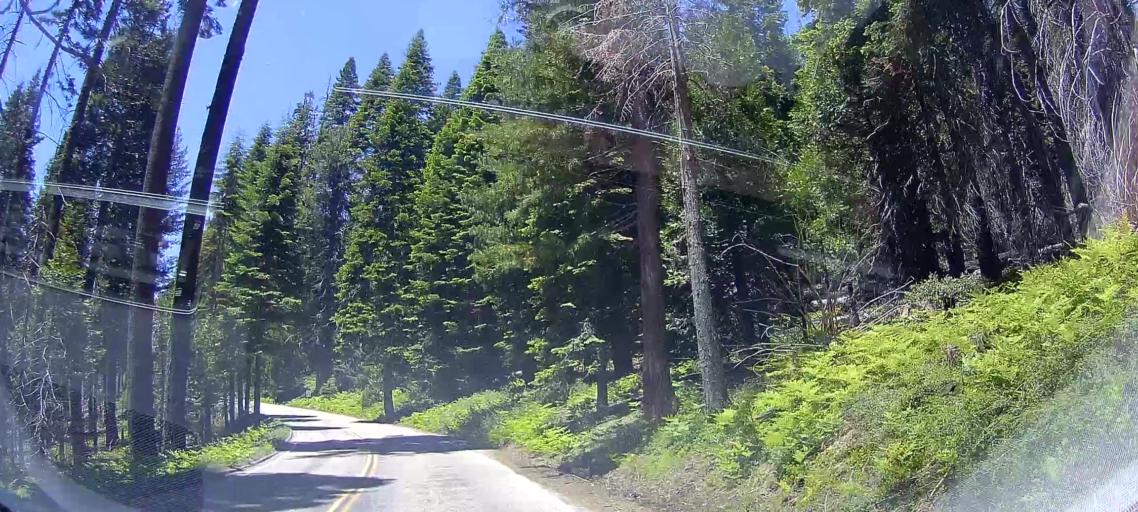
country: US
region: California
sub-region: Tulare County
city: Three Rivers
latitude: 36.6525
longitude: -118.8286
